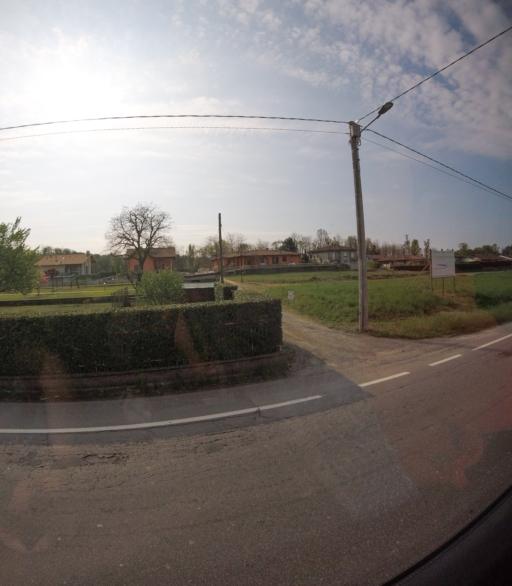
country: IT
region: Piedmont
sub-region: Provincia di Novara
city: Gattico
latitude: 45.7229
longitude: 8.4917
